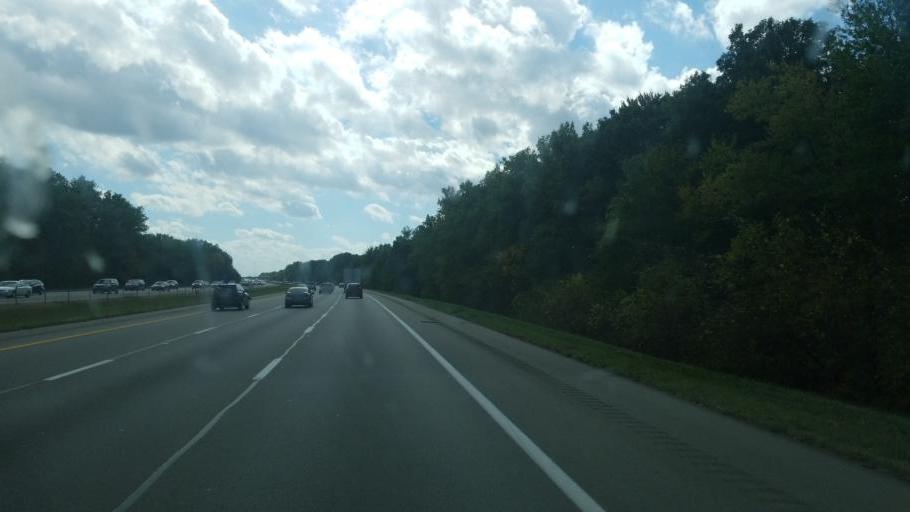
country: US
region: Ohio
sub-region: Delaware County
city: Sunbury
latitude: 40.2993
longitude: -82.9240
